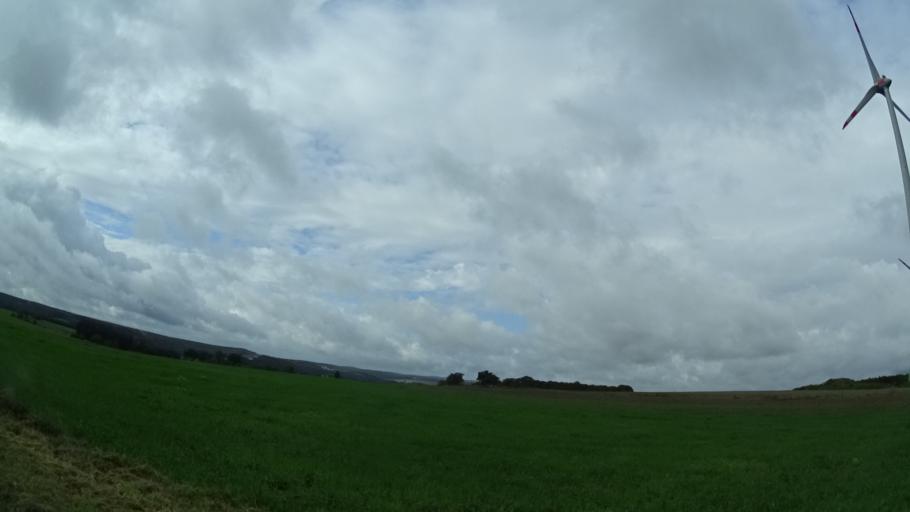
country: DE
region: Bavaria
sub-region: Upper Franconia
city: Priesendorf
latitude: 49.9072
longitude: 10.7363
